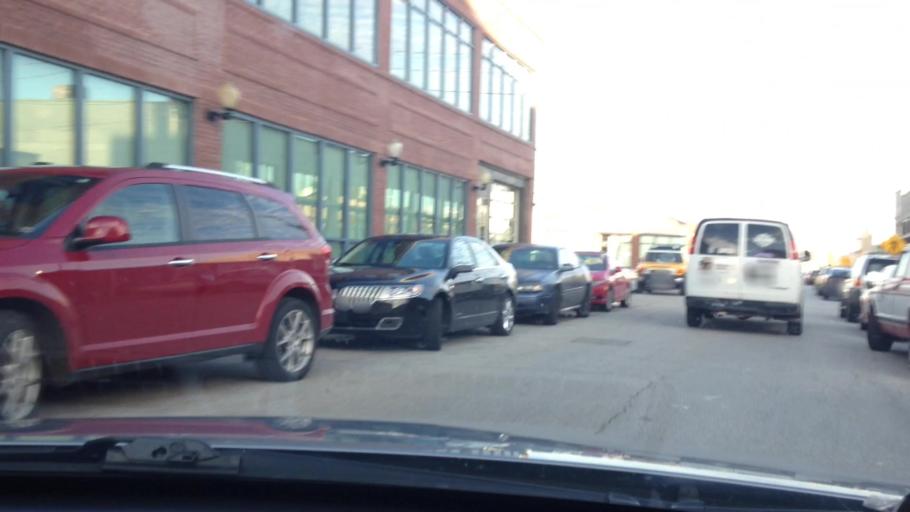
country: US
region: Missouri
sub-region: Jackson County
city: Kansas City
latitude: 39.0933
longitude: -94.5788
